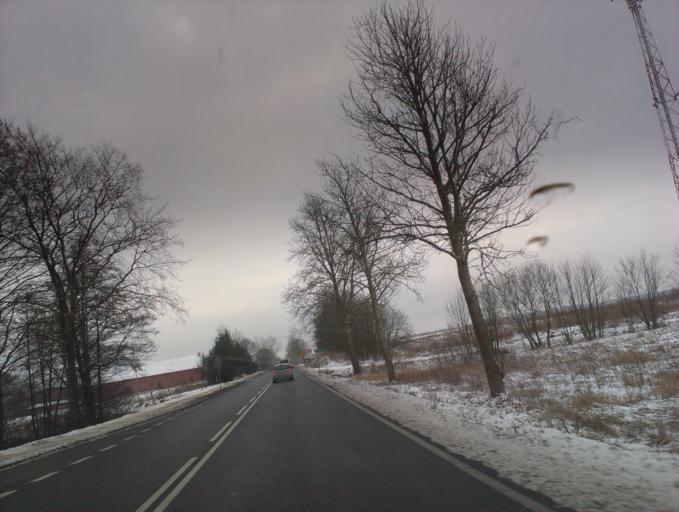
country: PL
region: West Pomeranian Voivodeship
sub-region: Powiat szczecinecki
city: Szczecinek
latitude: 53.6487
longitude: 16.7497
